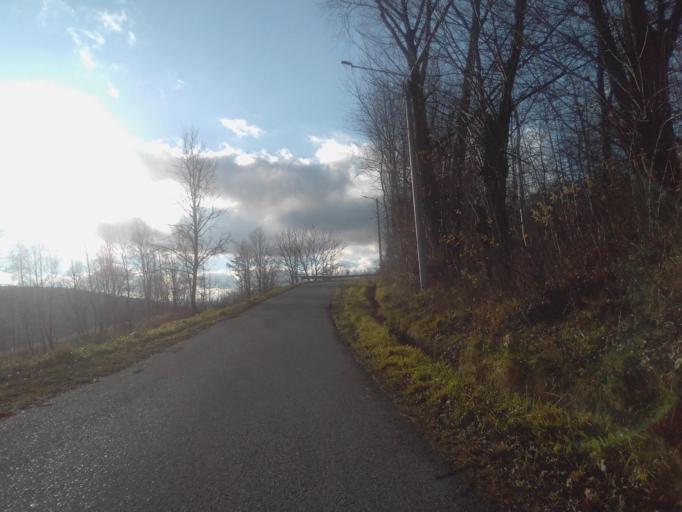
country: PL
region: Subcarpathian Voivodeship
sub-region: Powiat rzeszowski
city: Lubenia
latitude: 49.9373
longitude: 21.9014
